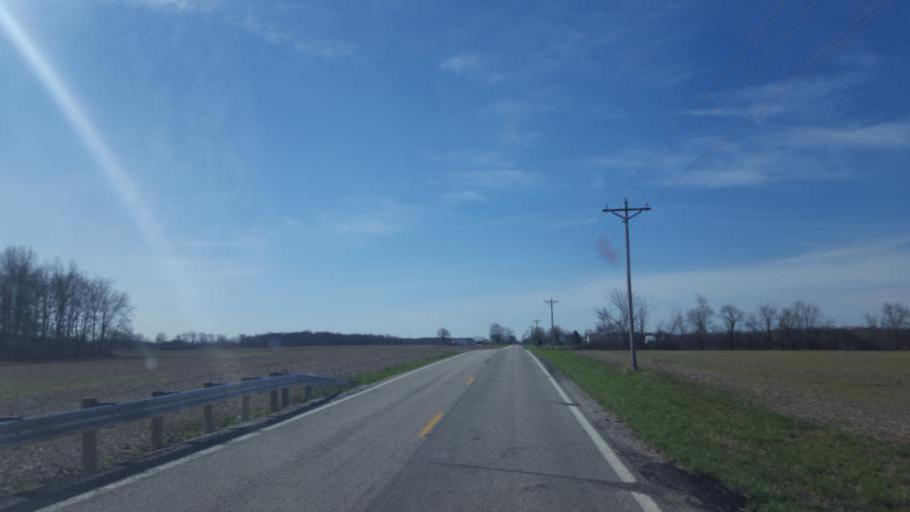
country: US
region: Ohio
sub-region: Morrow County
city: Cardington
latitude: 40.5741
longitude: -82.9622
